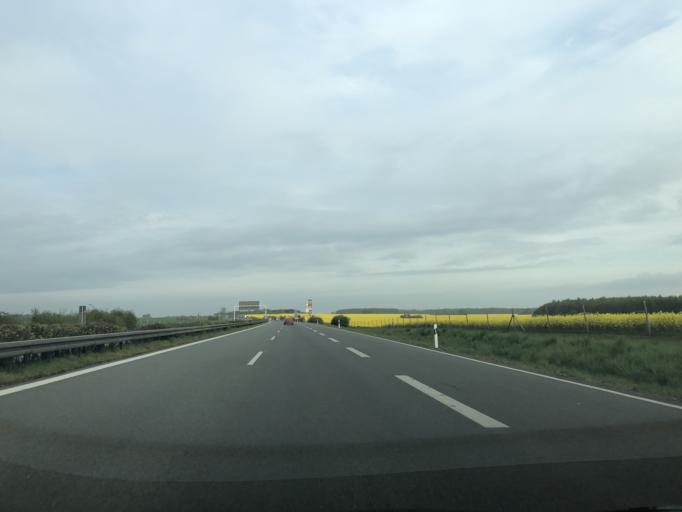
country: DE
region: Mecklenburg-Vorpommern
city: Grimmen
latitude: 54.0873
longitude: 13.1238
